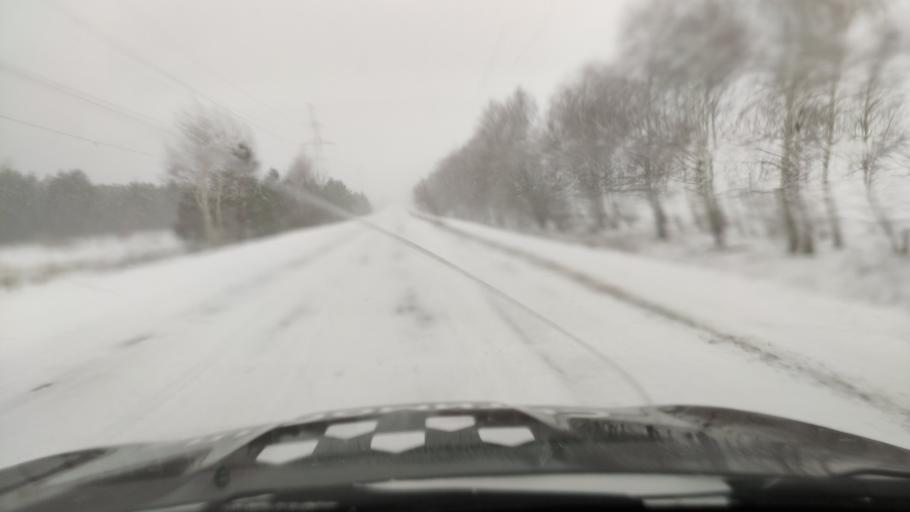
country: RU
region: Samara
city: Povolzhskiy
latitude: 53.5285
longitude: 49.7163
